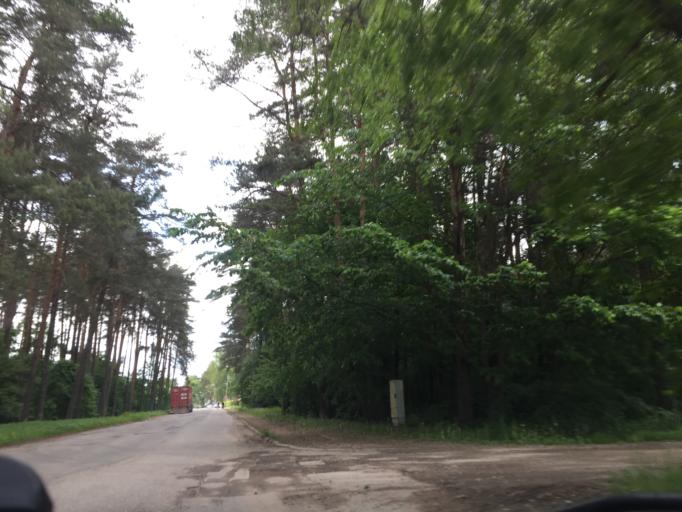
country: LV
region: Valmieras Rajons
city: Valmiera
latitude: 57.5234
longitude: 25.4309
